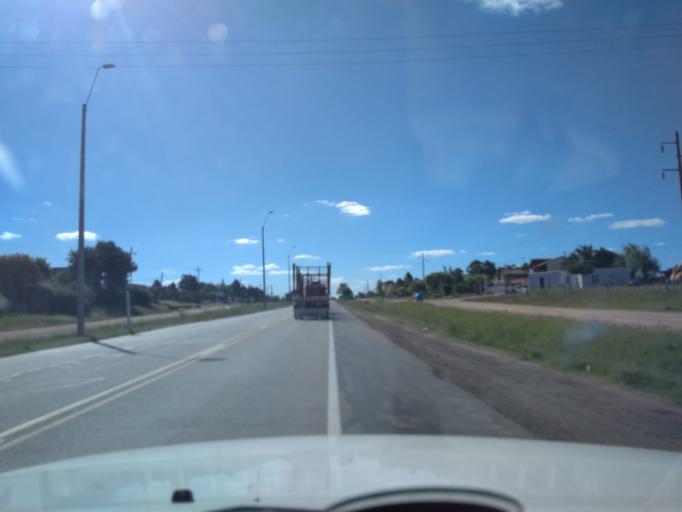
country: UY
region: Florida
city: Florida
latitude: -34.0837
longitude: -56.2139
